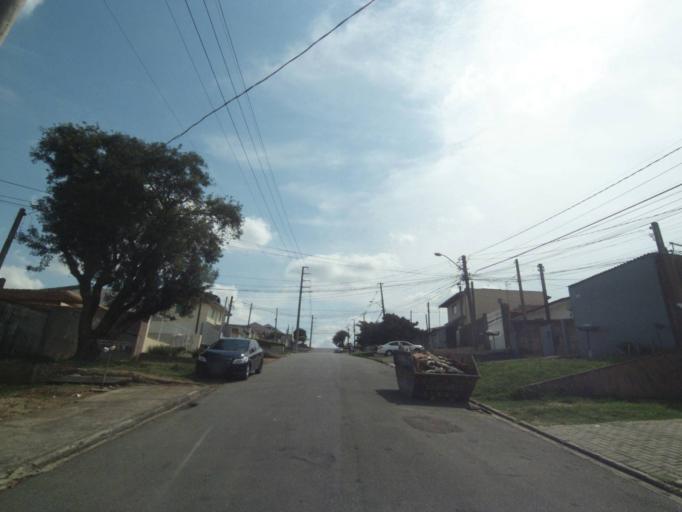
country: BR
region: Parana
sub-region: Pinhais
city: Pinhais
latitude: -25.4019
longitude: -49.1989
